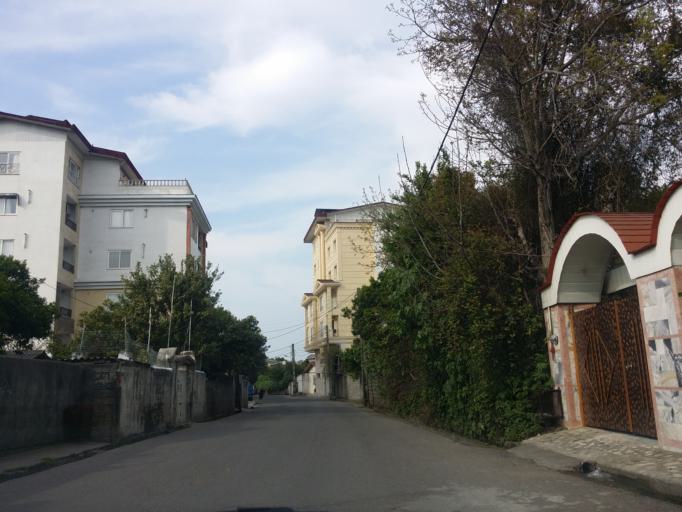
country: IR
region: Mazandaran
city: Chalus
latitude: 36.6546
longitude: 51.4134
